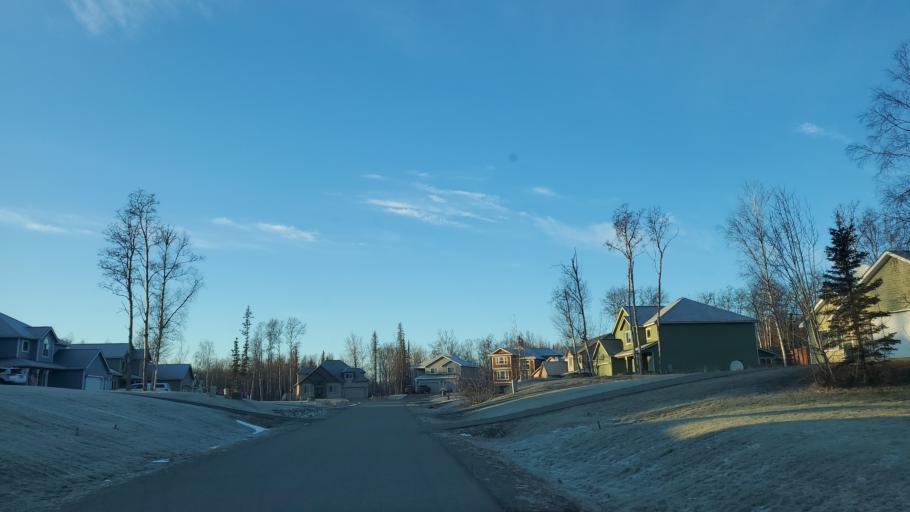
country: US
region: Alaska
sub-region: Matanuska-Susitna Borough
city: Wasilla
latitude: 61.5916
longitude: -149.4544
